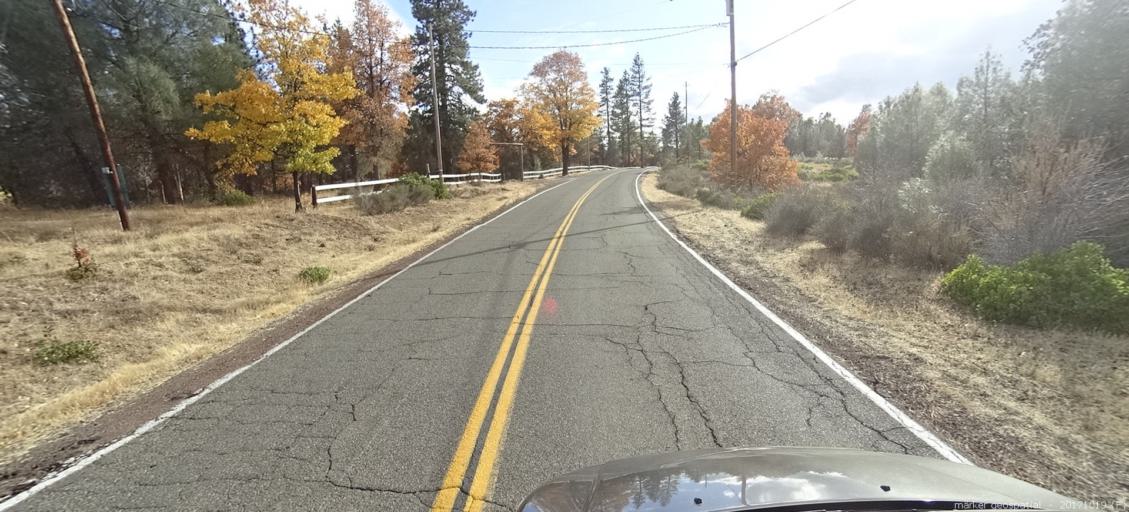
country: US
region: California
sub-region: Shasta County
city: Burney
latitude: 40.9641
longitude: -121.4354
